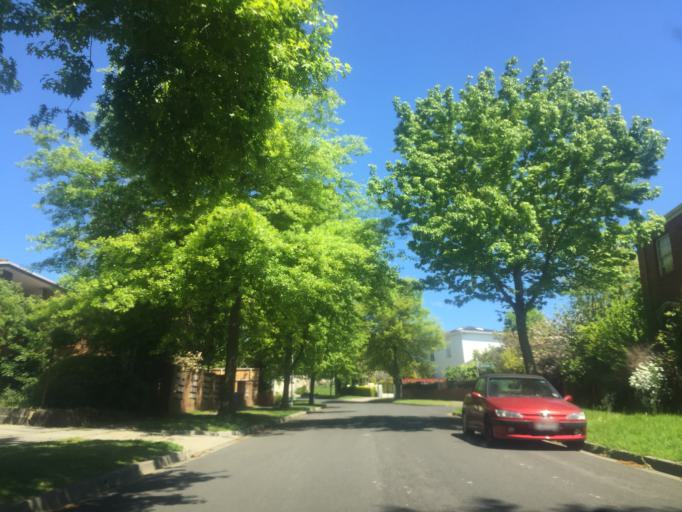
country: AU
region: Victoria
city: Mont Albert
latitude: -37.8077
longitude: 145.0878
